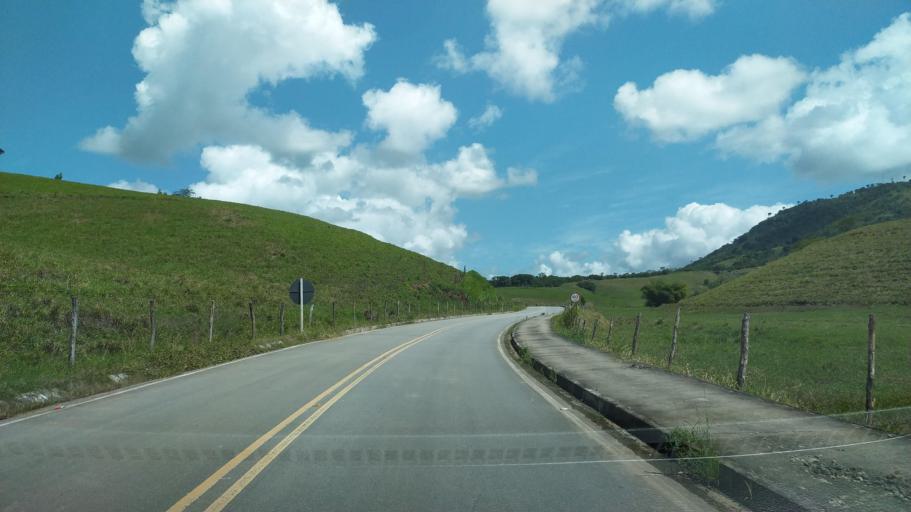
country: BR
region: Alagoas
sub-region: Uniao Dos Palmares
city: Uniao dos Palmares
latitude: -9.1643
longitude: -36.0542
